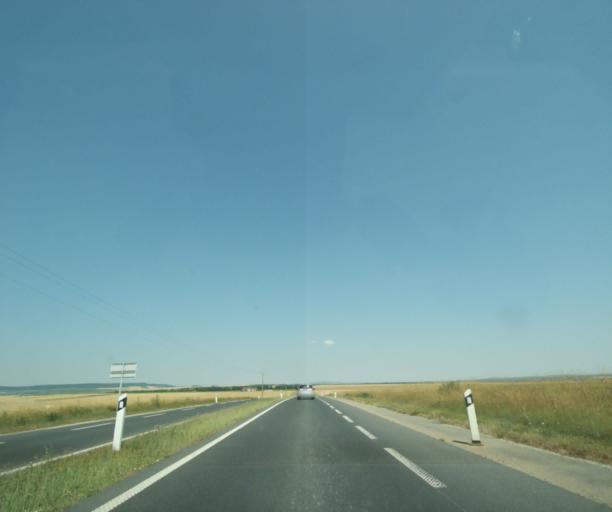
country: FR
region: Champagne-Ardenne
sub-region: Departement de la Marne
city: Mourmelon-le-Grand
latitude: 49.0765
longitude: 4.2861
